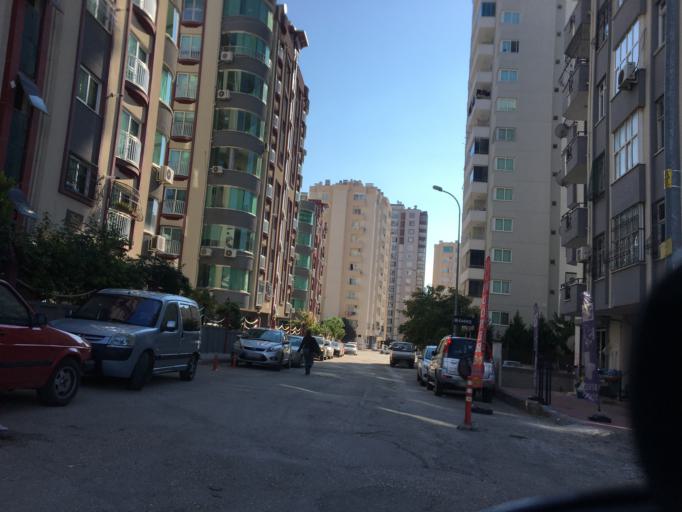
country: TR
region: Adana
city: Seyhan
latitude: 37.0277
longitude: 35.2850
